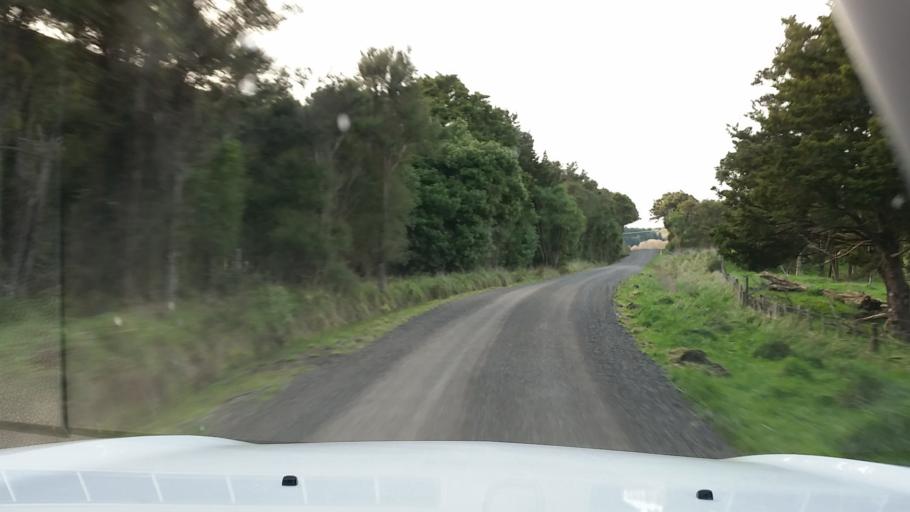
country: NZ
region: Wellington
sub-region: Masterton District
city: Masterton
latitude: -41.1868
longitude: 175.9508
